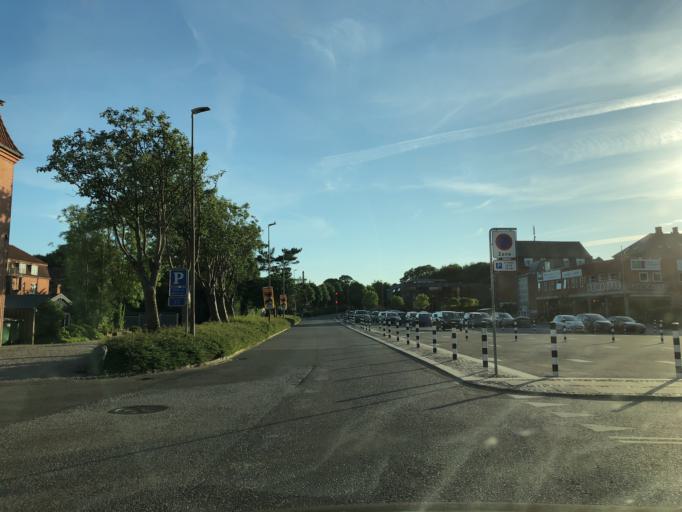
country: DK
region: Central Jutland
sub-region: Struer Kommune
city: Struer
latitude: 56.4914
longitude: 8.5924
